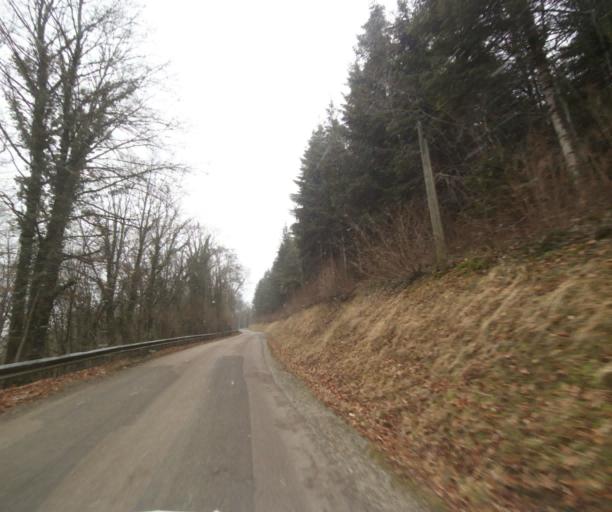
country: FR
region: Champagne-Ardenne
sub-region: Departement de la Haute-Marne
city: Chevillon
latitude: 48.5226
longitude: 5.0911
